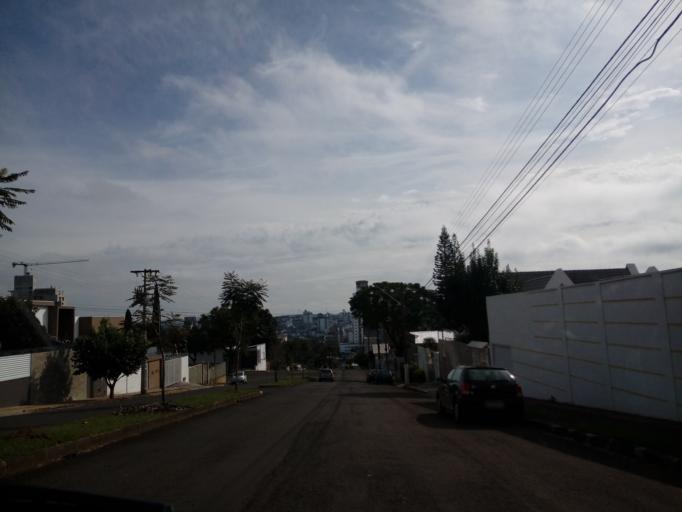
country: BR
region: Santa Catarina
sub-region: Chapeco
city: Chapeco
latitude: -27.1057
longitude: -52.6234
